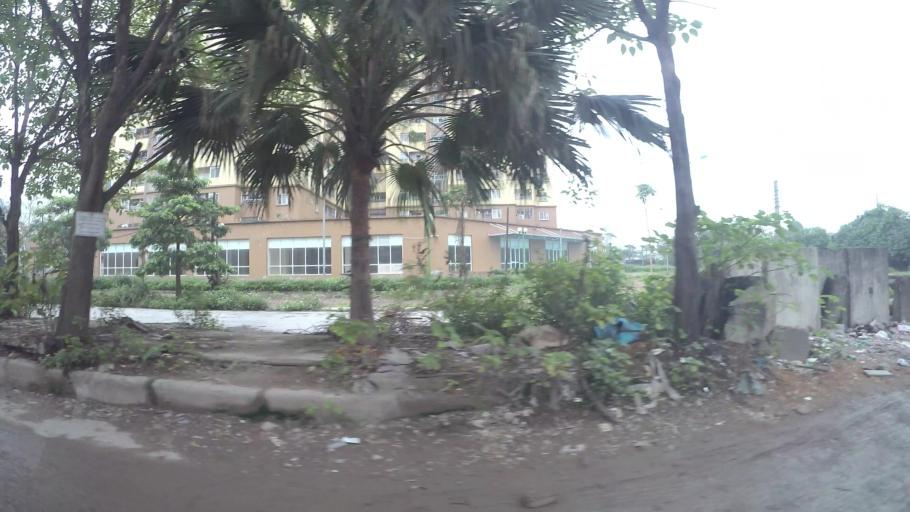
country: VN
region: Ha Noi
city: Hai BaTrung
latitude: 20.9837
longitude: 105.8696
